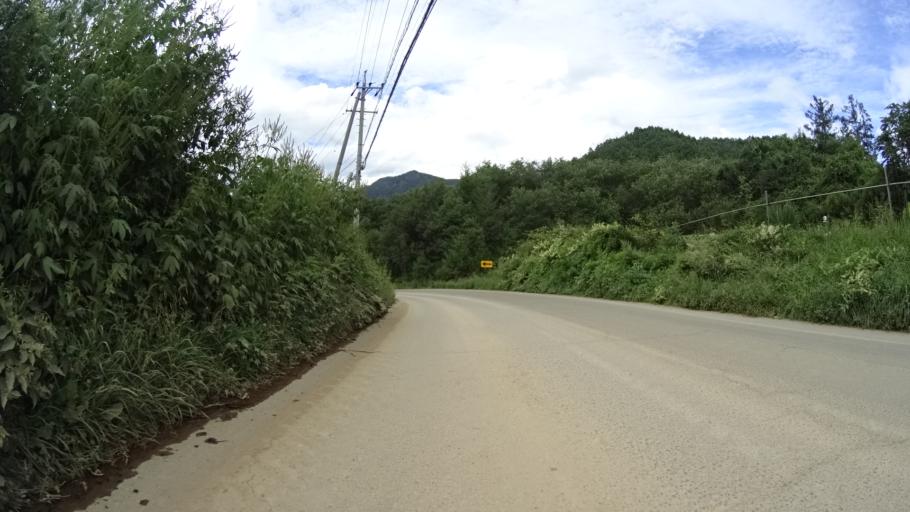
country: JP
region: Nagano
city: Saku
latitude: 35.9594
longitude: 138.5475
